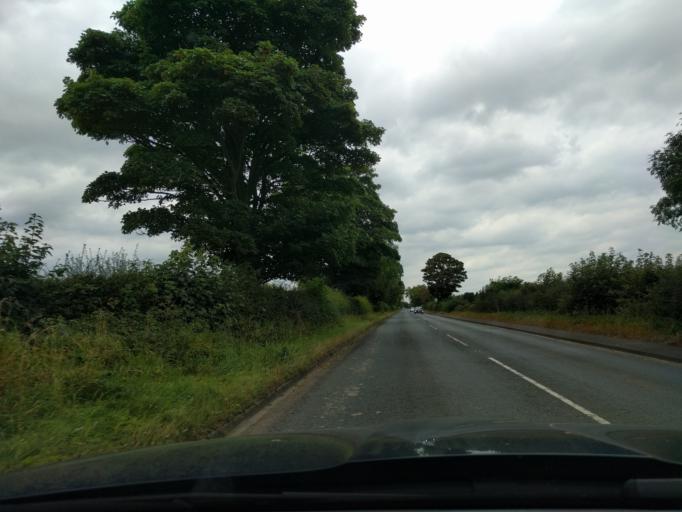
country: GB
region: England
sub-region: Northumberland
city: Morpeth
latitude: 55.1525
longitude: -1.6667
